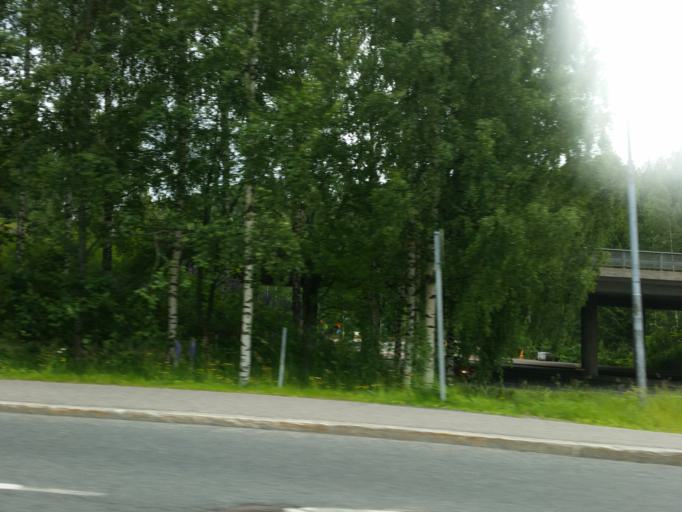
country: FI
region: Northern Savo
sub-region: Kuopio
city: Kuopio
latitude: 62.8953
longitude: 27.6484
